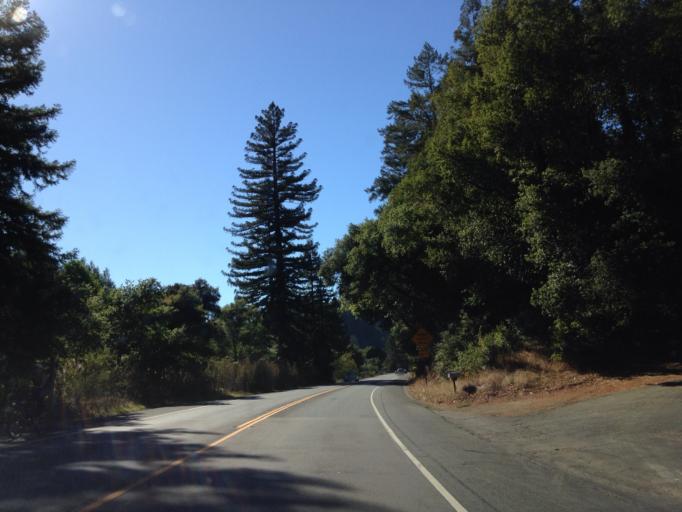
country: US
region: California
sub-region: Sonoma County
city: Guerneville
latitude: 38.5058
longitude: -122.9579
